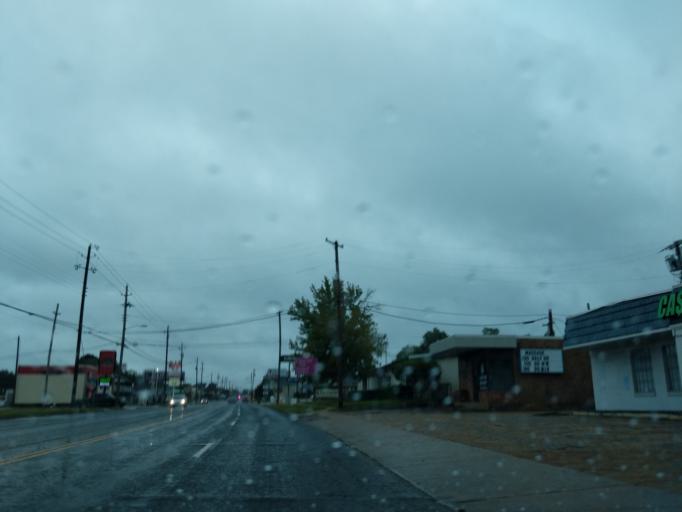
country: US
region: Texas
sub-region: Nacogdoches County
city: Nacogdoches
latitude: 31.6259
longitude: -94.6522
